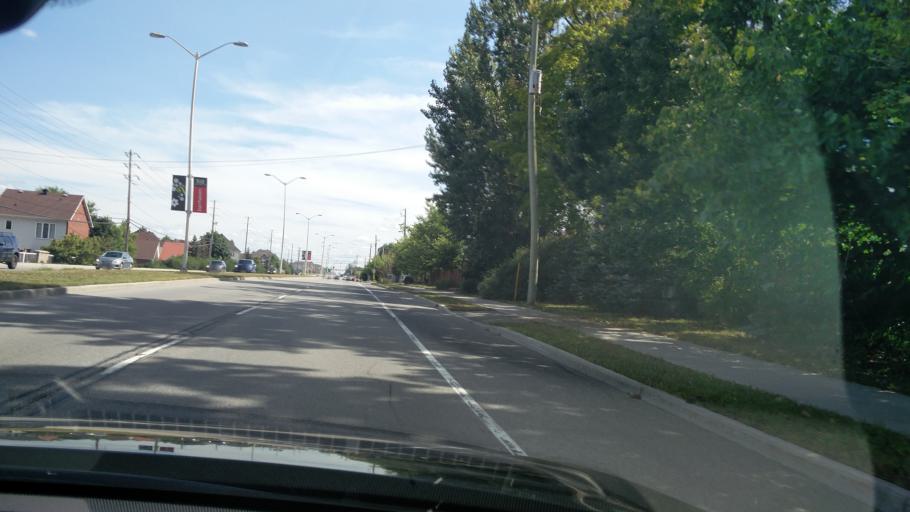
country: CA
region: Ontario
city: Bells Corners
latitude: 45.2799
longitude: -75.7211
